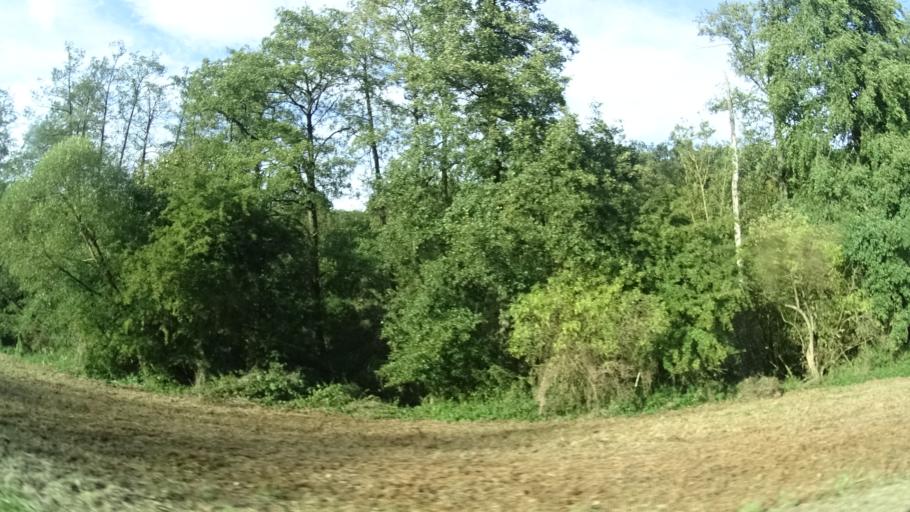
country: DE
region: Hesse
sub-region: Regierungsbezirk Kassel
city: Eichenzell
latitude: 50.5158
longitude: 9.6880
